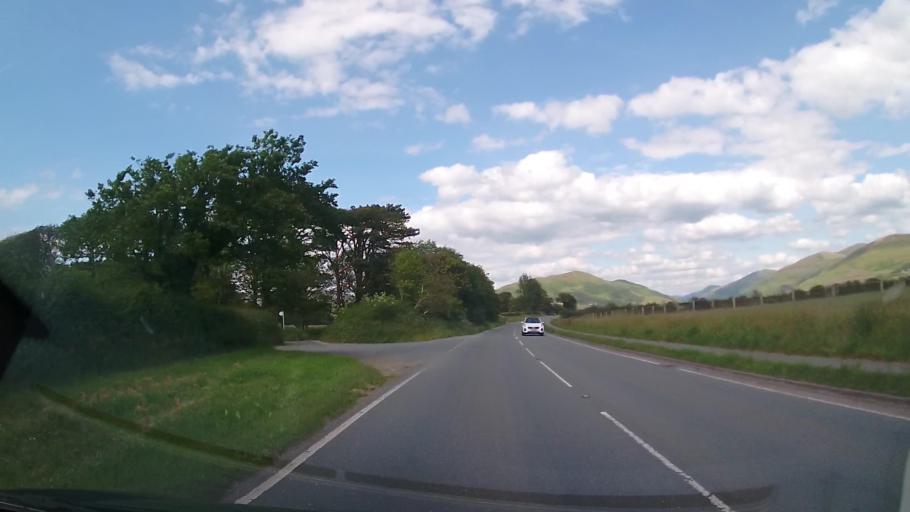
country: GB
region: Wales
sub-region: Gwynedd
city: Tywyn
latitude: 52.5951
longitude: -4.0713
